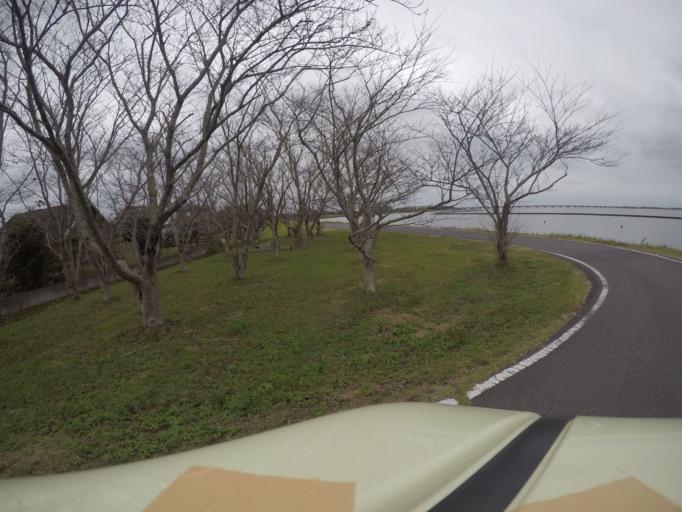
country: JP
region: Ibaraki
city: Ishioka
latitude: 36.1041
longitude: 140.3988
